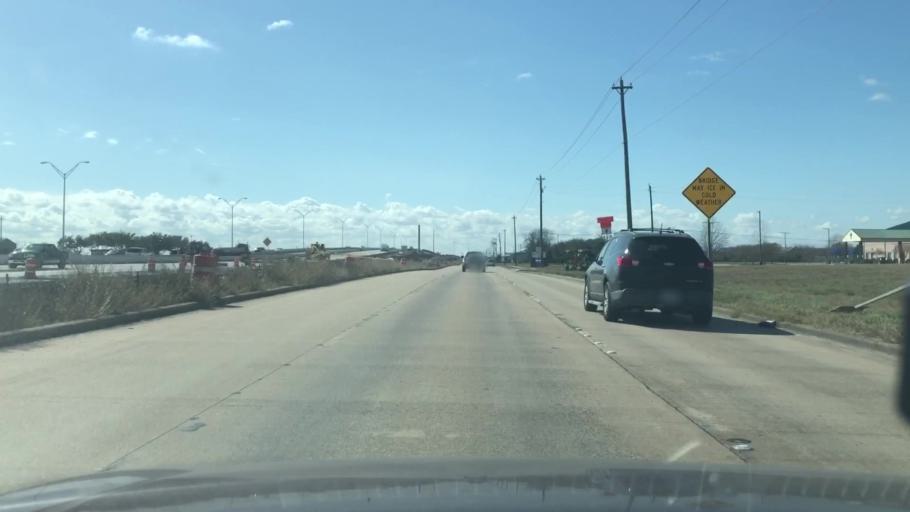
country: US
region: Texas
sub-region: Harris County
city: Pasadena
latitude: 29.6370
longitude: -95.1645
